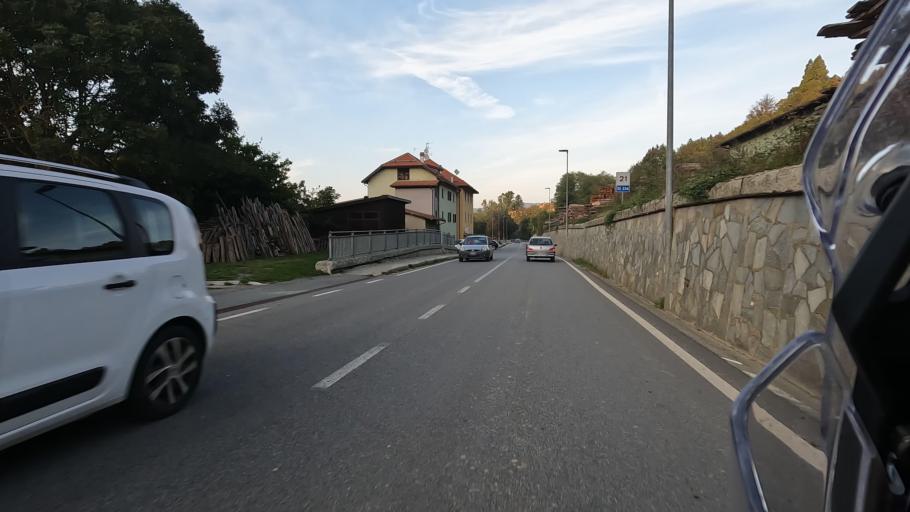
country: IT
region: Liguria
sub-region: Provincia di Savona
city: Sassello
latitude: 44.4722
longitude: 8.4853
